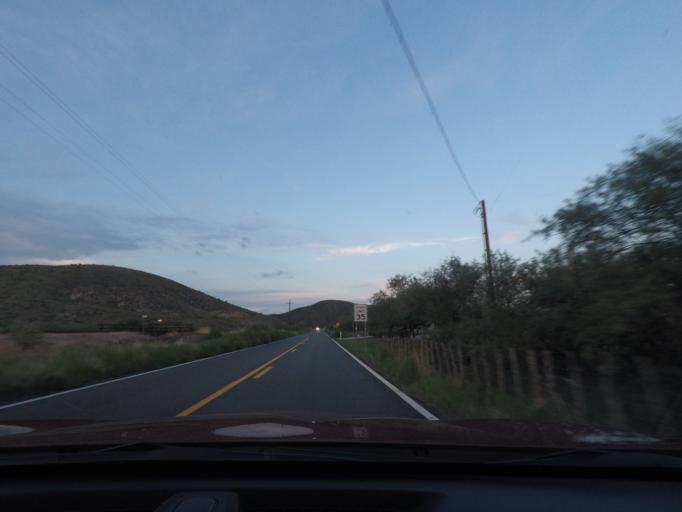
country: US
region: Arizona
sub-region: Yavapai County
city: Prescott
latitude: 34.4181
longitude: -112.7079
